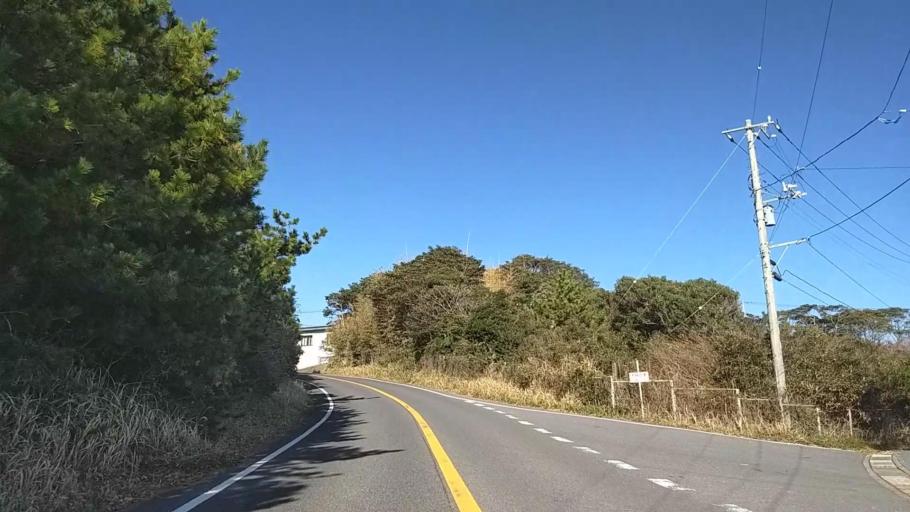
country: JP
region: Chiba
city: Hasaki
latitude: 35.7030
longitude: 140.8622
